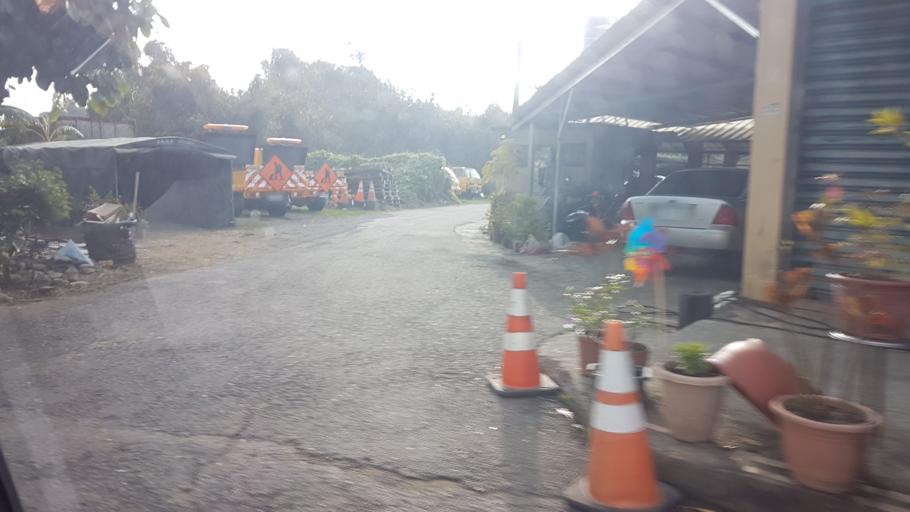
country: TW
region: Taiwan
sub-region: Chiayi
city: Jiayi Shi
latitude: 23.3808
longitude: 120.4391
